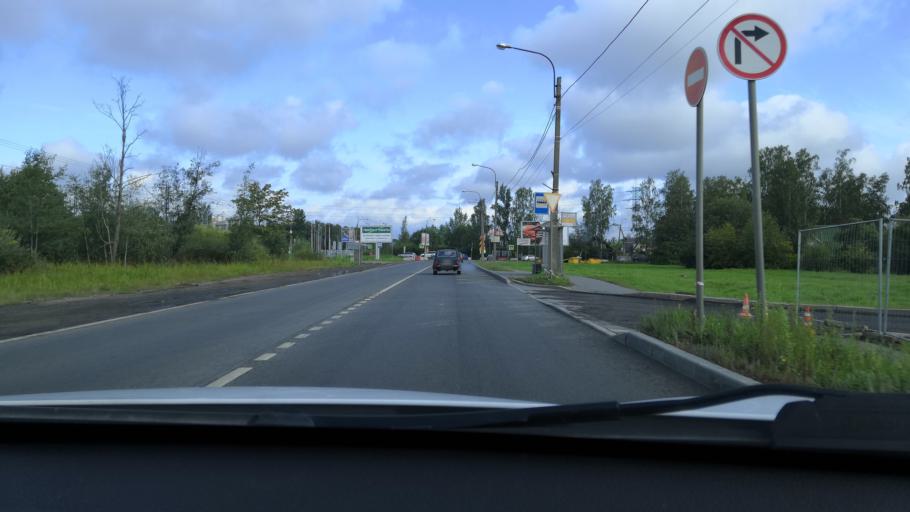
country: RU
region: St.-Petersburg
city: Tyarlevo
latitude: 59.7113
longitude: 30.4361
